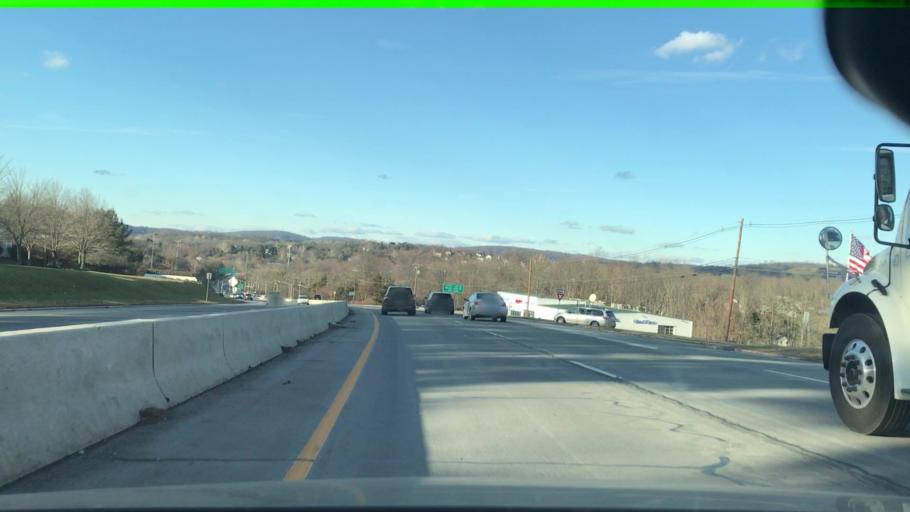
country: US
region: New Jersey
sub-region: Hunterdon County
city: Annandale
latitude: 40.6308
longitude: -74.8819
